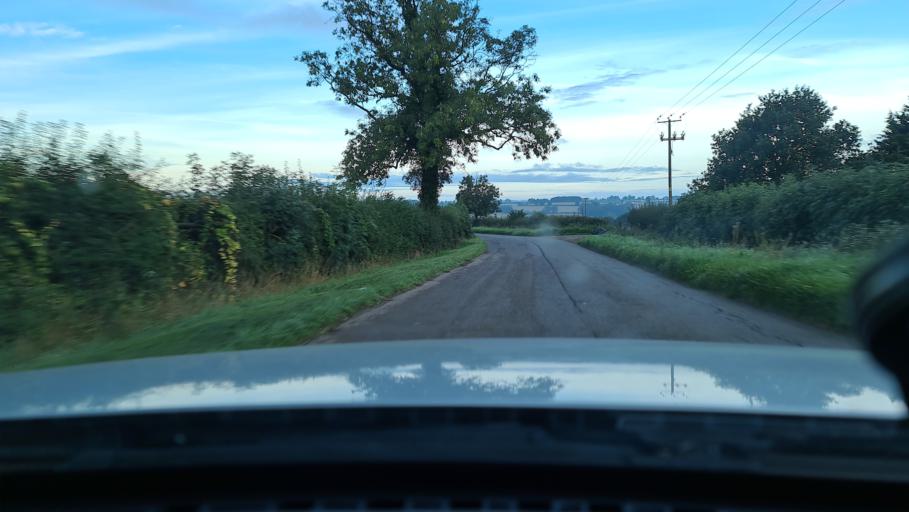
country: GB
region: England
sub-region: Oxfordshire
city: Hanwell
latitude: 52.1016
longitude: -1.3432
